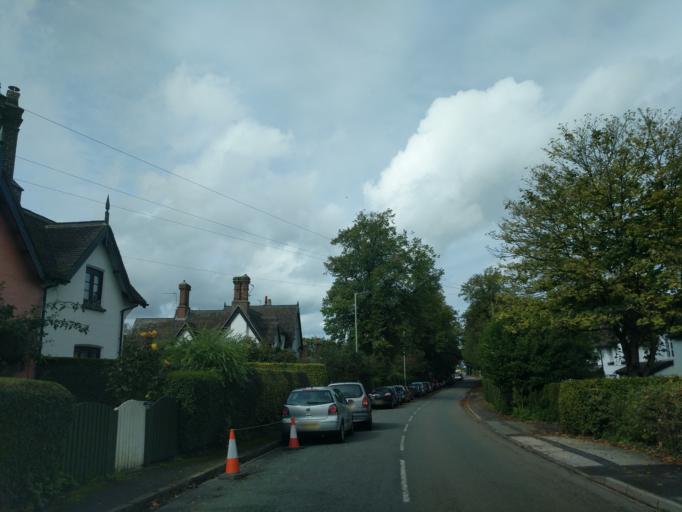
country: GB
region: England
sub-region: Staffordshire
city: Audley
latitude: 53.0041
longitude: -2.2879
